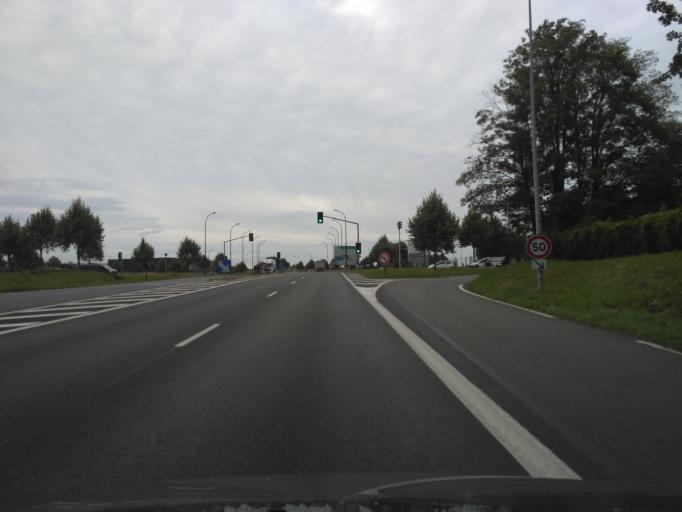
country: FR
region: Ile-de-France
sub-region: Departement de Seine-et-Marne
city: Rubelles
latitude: 48.5435
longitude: 2.6800
